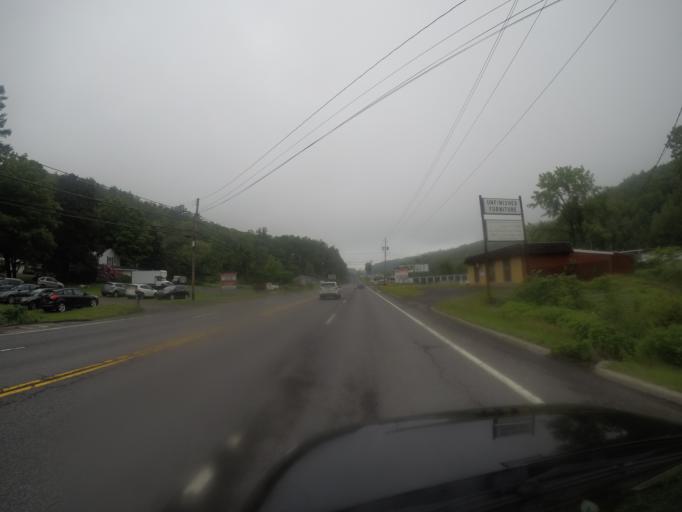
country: US
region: New York
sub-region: Ulster County
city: Hurley
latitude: 41.9608
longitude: -74.0574
